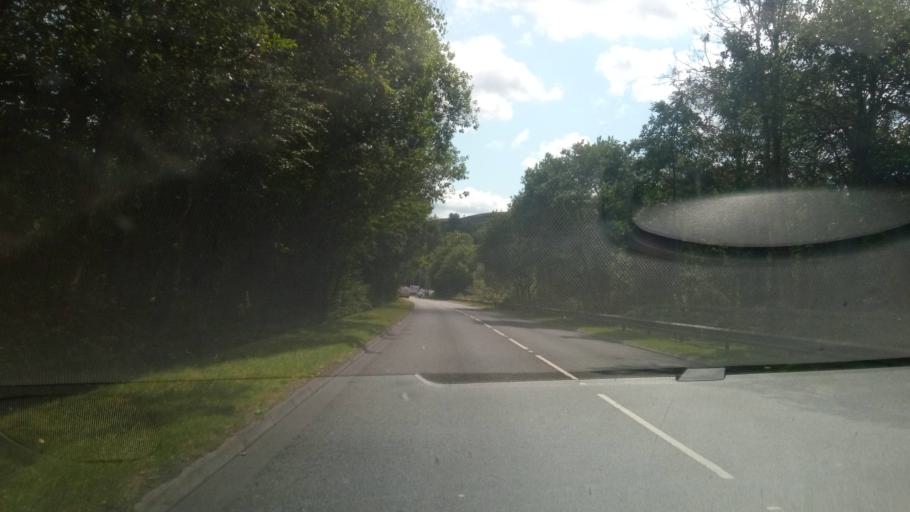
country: GB
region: Wales
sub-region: Rhondda Cynon Taf
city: Tonypandy
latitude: 51.6191
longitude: -3.4478
